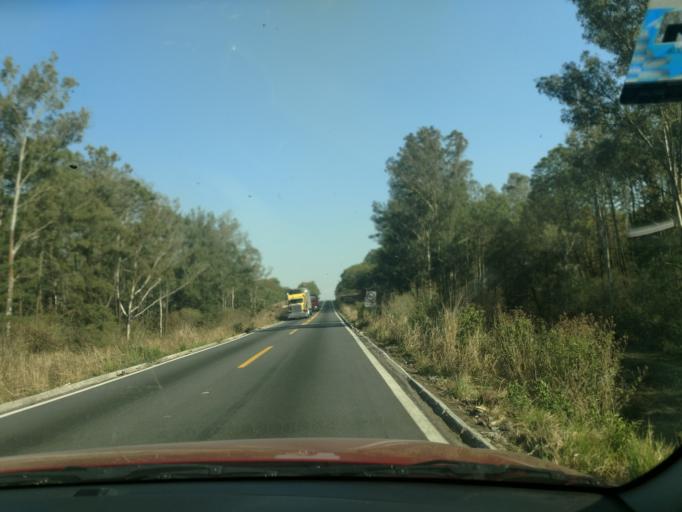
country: MX
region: Nayarit
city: Santa Maria del Oro
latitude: 21.2739
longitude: -104.6486
